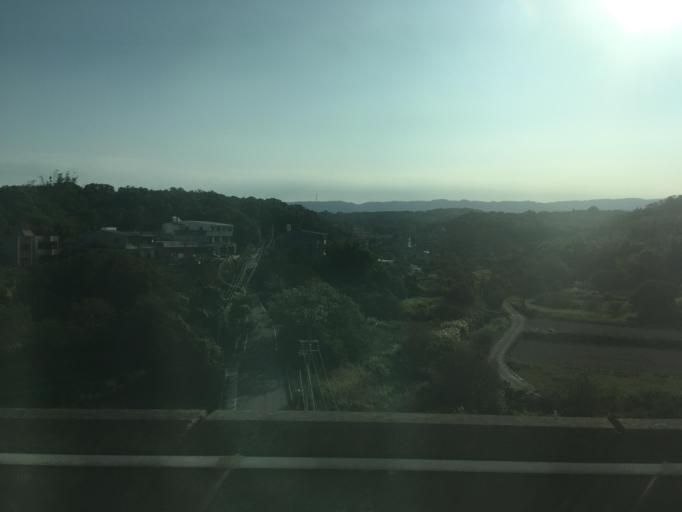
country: TW
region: Taiwan
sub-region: Miaoli
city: Miaoli
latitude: 24.4421
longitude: 120.6990
